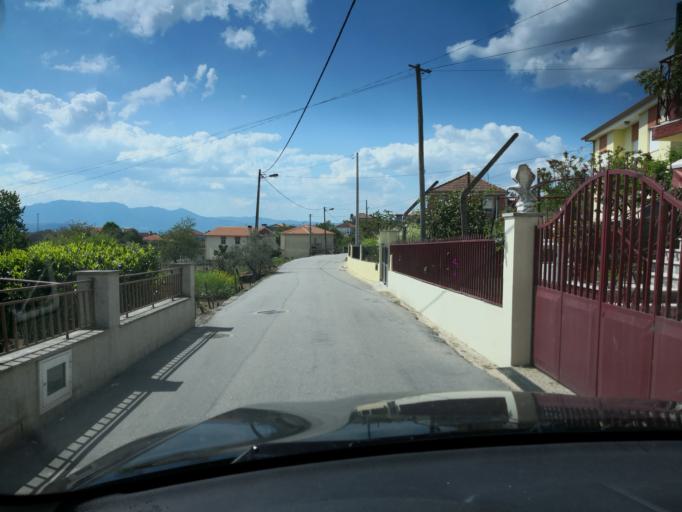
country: PT
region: Vila Real
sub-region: Sabrosa
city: Vilela
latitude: 41.2247
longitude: -7.6919
